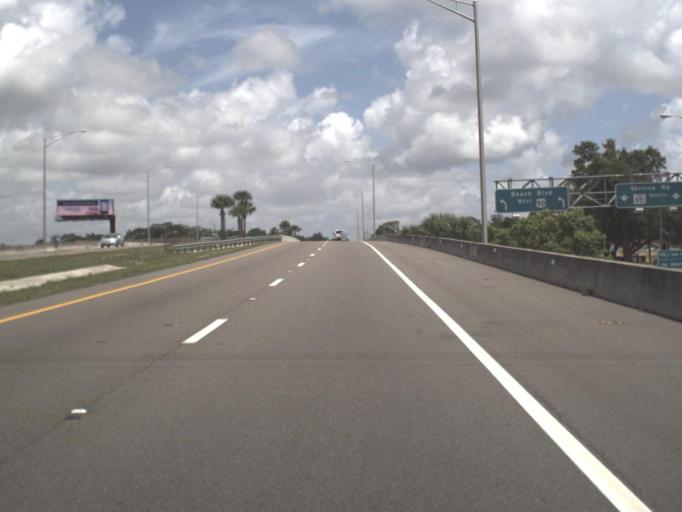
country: US
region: Florida
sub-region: Duval County
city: Jacksonville
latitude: 30.2850
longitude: -81.5590
